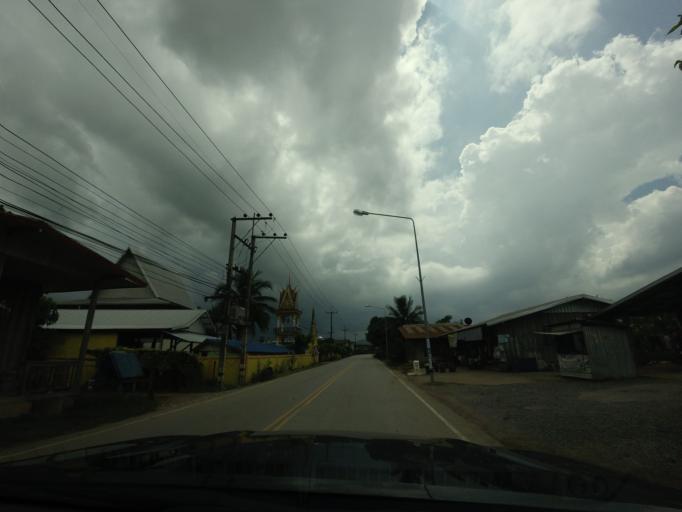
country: LA
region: Vientiane
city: Muang Sanakham
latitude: 17.9999
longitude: 101.7555
